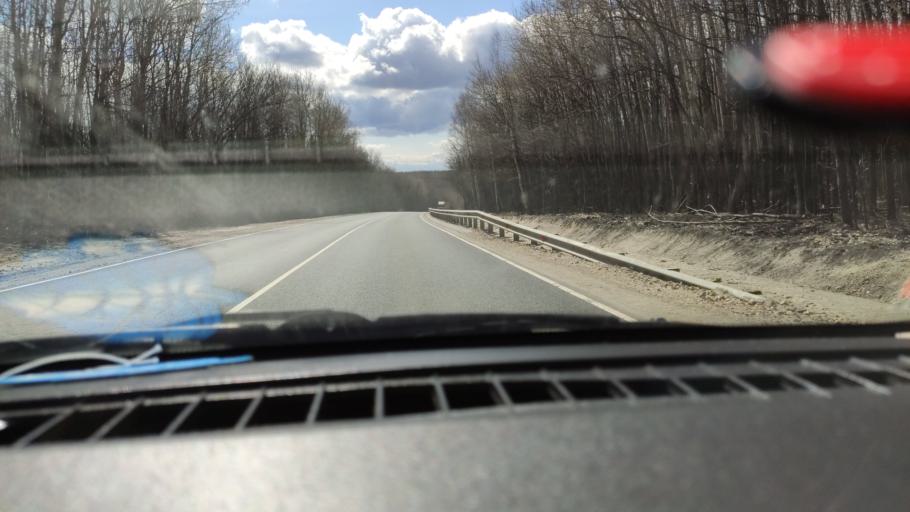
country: RU
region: Saratov
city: Khvalynsk
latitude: 52.4590
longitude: 48.0166
